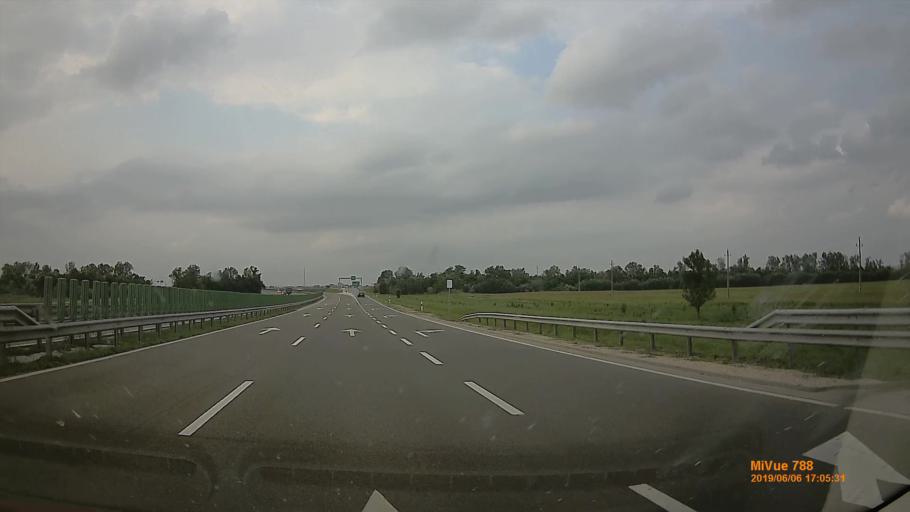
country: HU
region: Fejer
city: Szekesfehervar
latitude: 47.1762
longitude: 18.3801
